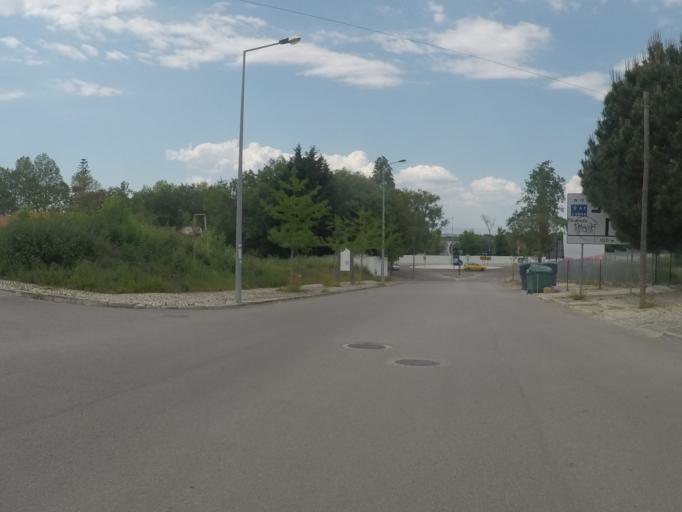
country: PT
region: Setubal
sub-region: Palmela
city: Quinta do Anjo
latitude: 38.5193
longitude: -9.0096
